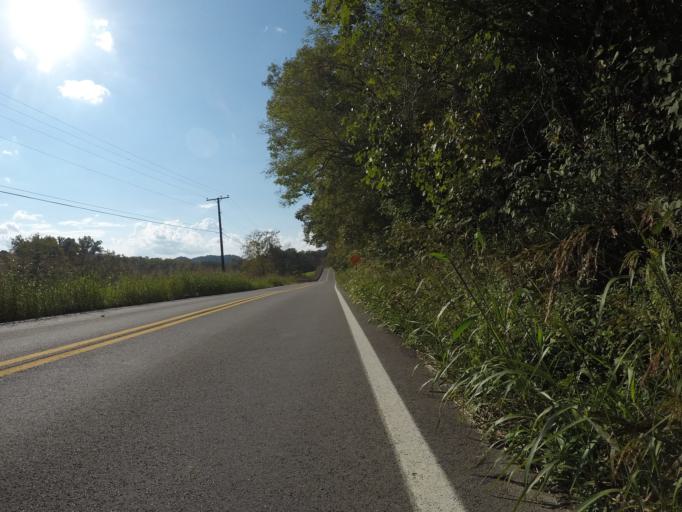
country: US
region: Ohio
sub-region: Lawrence County
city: Burlington
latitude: 38.3723
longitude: -82.5172
